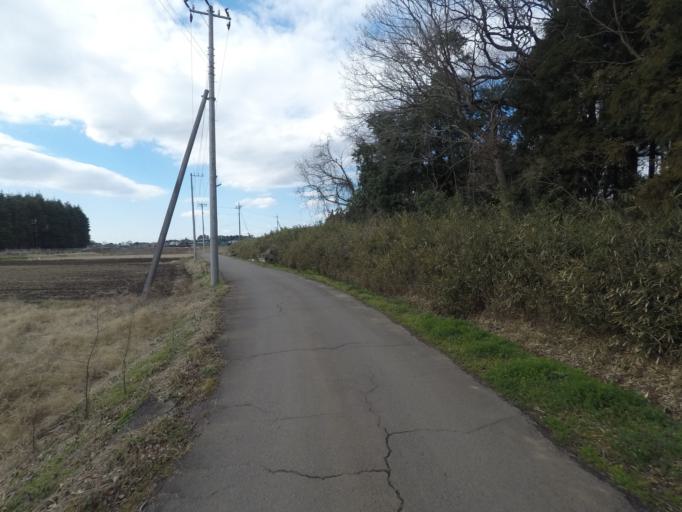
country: JP
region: Ibaraki
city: Ushiku
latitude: 36.0138
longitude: 140.1143
